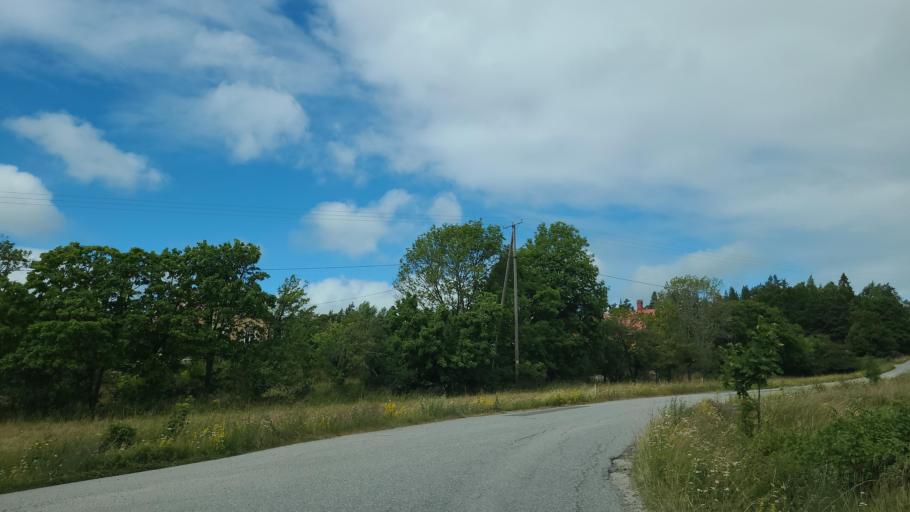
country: FI
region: Varsinais-Suomi
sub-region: Aboland-Turunmaa
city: Nagu
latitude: 60.1674
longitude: 21.9808
